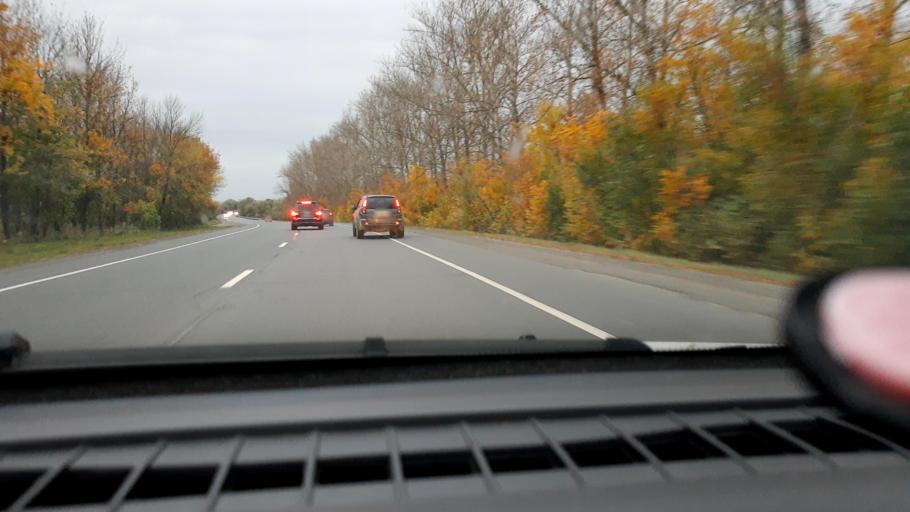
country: RU
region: Vladimir
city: Bogolyubovo
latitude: 56.2087
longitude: 40.5703
